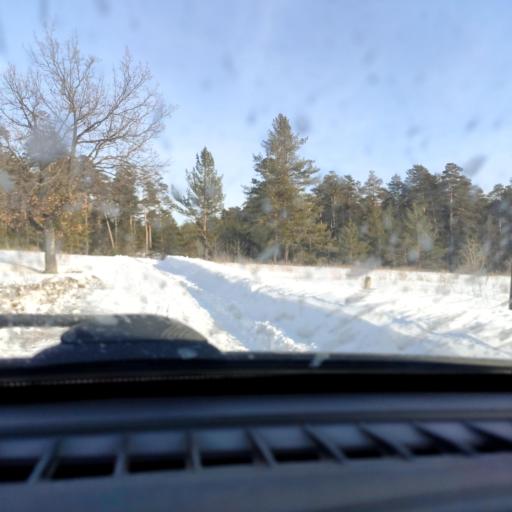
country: RU
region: Samara
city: Zhigulevsk
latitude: 53.4798
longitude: 49.5414
